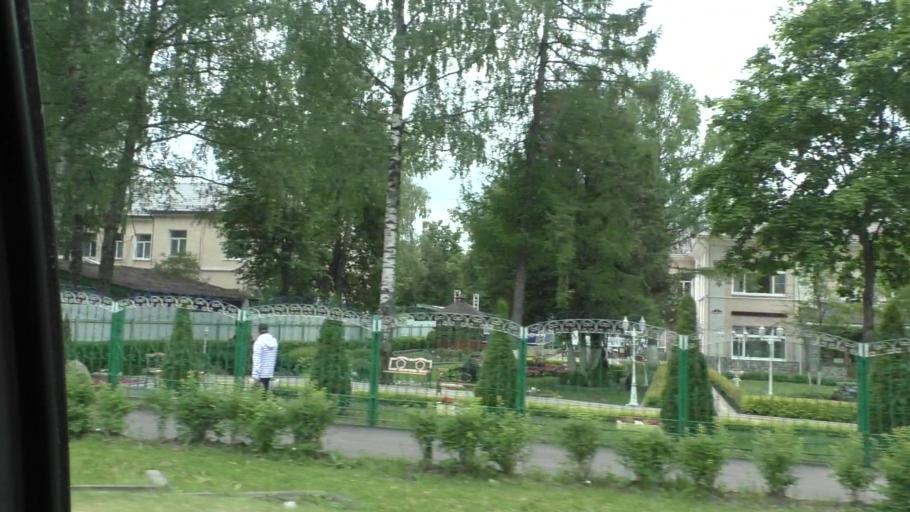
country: RU
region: Moskovskaya
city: Yegor'yevsk
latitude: 55.3915
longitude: 39.0232
